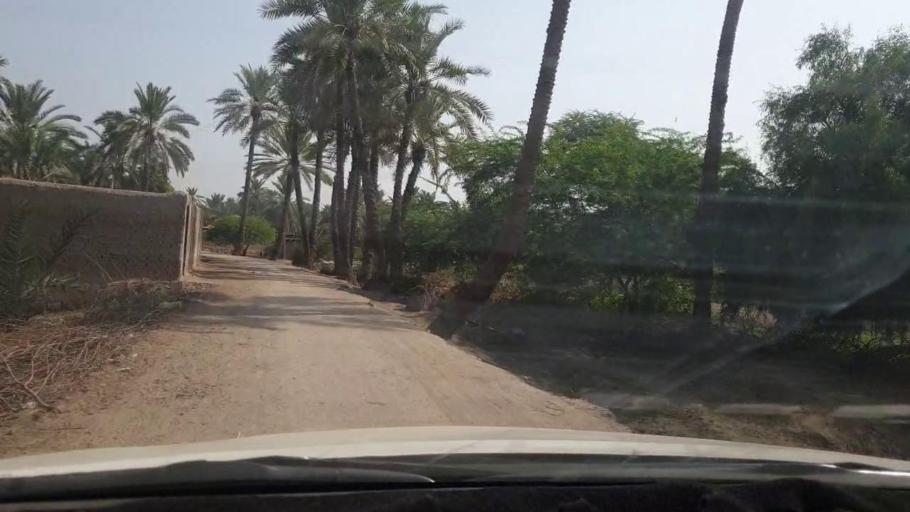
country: PK
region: Sindh
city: Rohri
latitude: 27.6017
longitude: 68.8907
